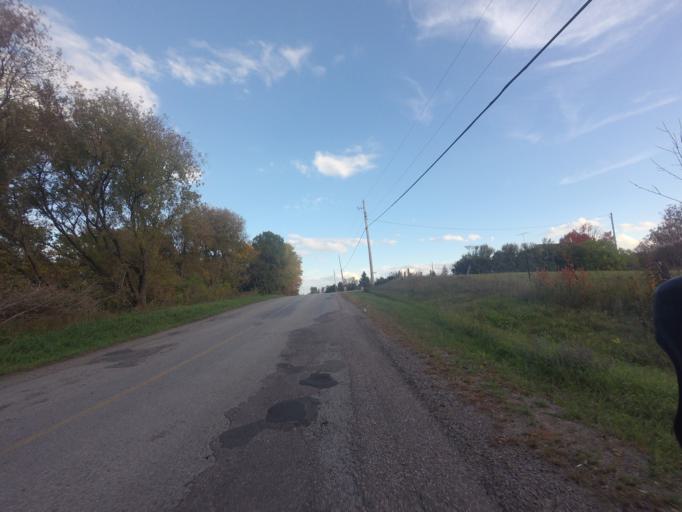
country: CA
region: Ontario
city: Pembroke
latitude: 45.5258
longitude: -77.0838
